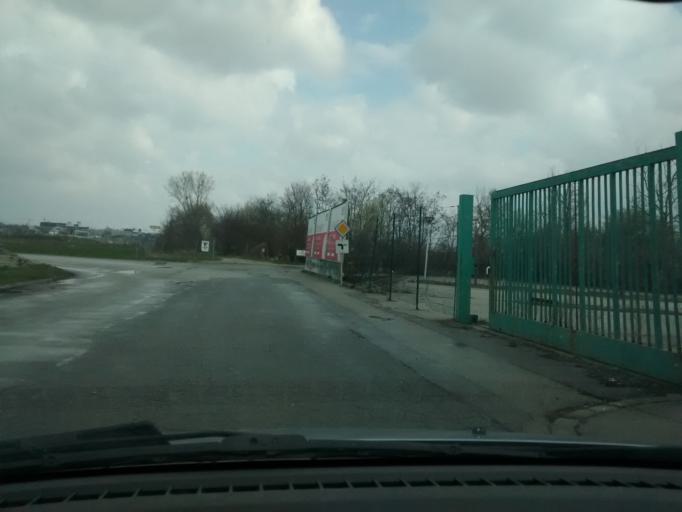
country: AT
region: Lower Austria
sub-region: Politischer Bezirk Modling
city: Wiener Neudorf
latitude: 48.0939
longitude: 16.3196
